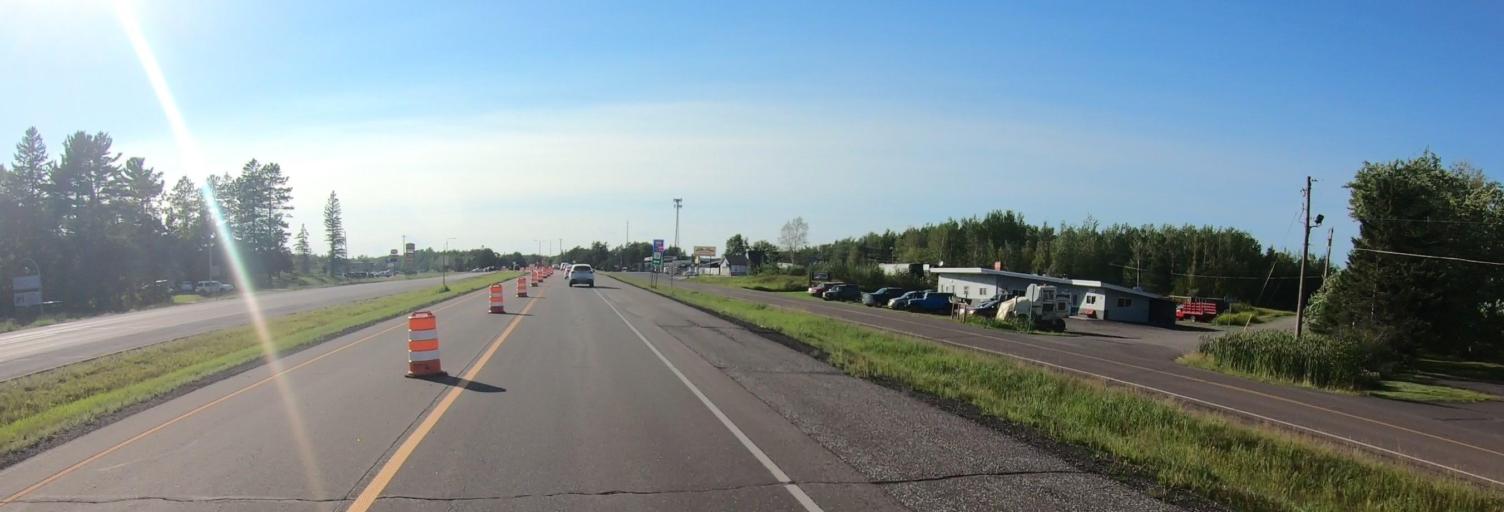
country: US
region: Minnesota
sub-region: Saint Louis County
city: Hermantown
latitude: 46.8492
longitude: -92.2776
